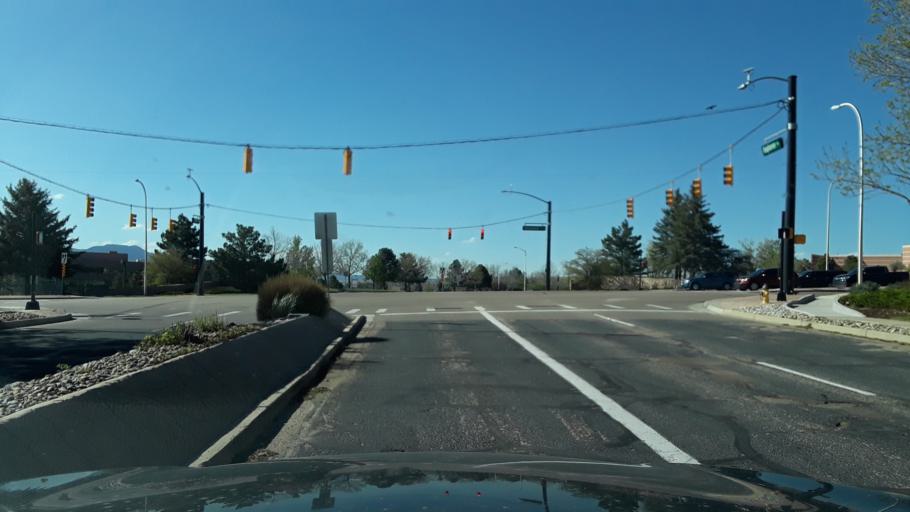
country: US
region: Colorado
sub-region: El Paso County
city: Air Force Academy
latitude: 38.9593
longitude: -104.7913
